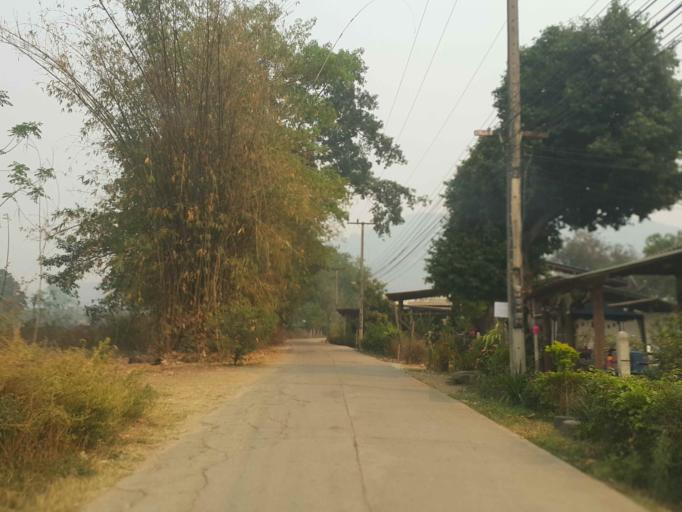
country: TH
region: Chiang Mai
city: Mae Taeng
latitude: 19.2182
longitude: 98.8526
